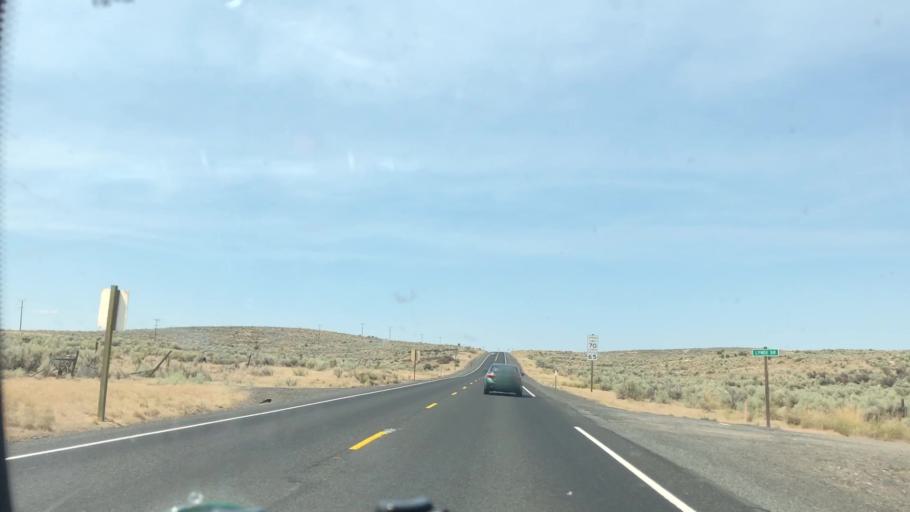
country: US
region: Idaho
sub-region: Owyhee County
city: Murphy
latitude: 42.9878
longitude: -117.0560
